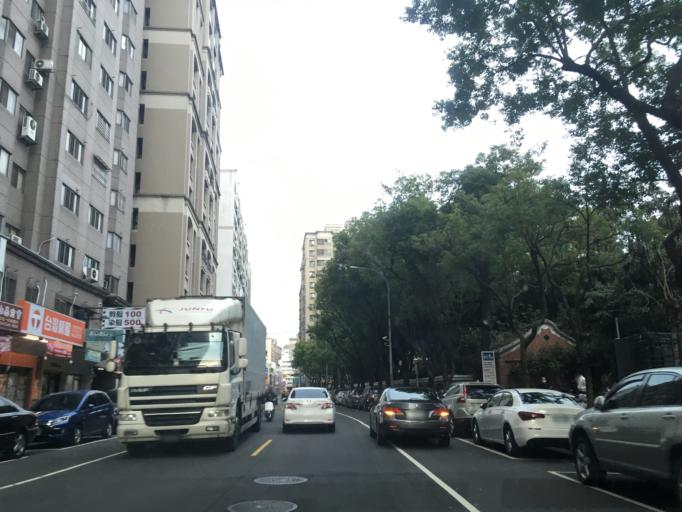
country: TW
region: Taiwan
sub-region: Taichung City
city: Taichung
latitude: 24.1757
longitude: 120.6866
